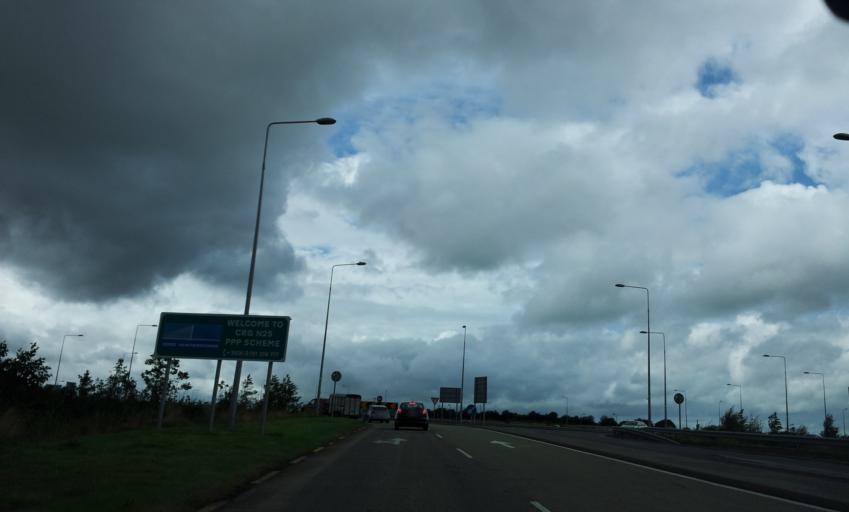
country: IE
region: Munster
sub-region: Waterford
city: Waterford
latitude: 52.2814
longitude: -7.1433
